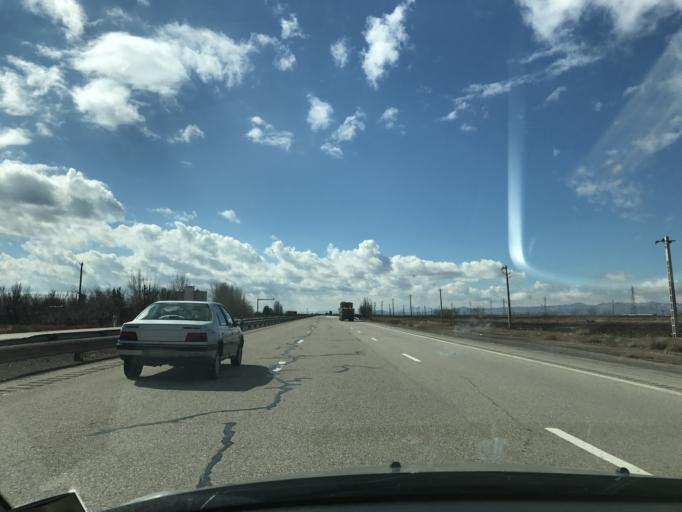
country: IR
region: Qazvin
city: Qazvin
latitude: 36.2356
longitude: 49.9042
